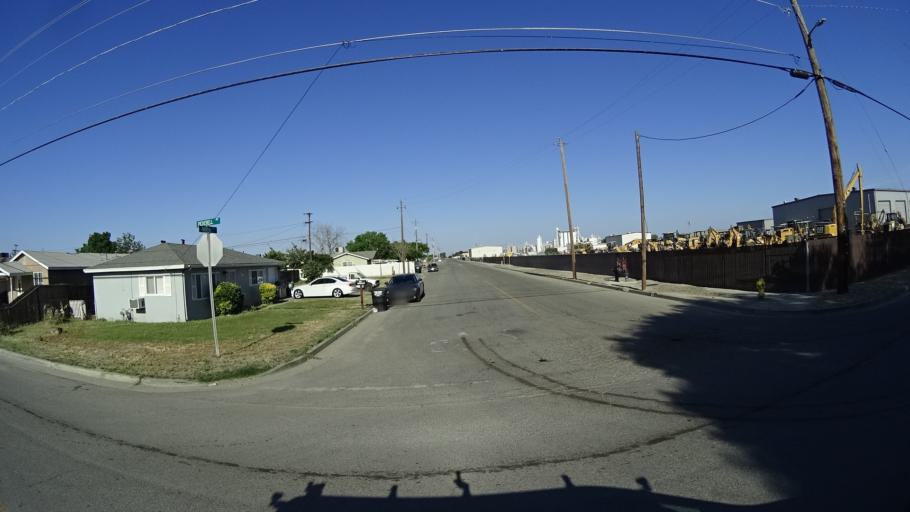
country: US
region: California
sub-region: Kings County
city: Corcoran
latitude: 36.1050
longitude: -119.5543
